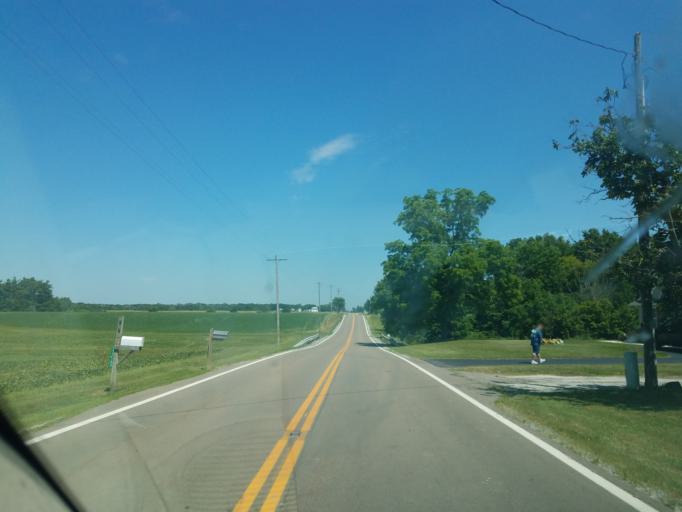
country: US
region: Ohio
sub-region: Wyandot County
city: Upper Sandusky
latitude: 40.8029
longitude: -83.3729
